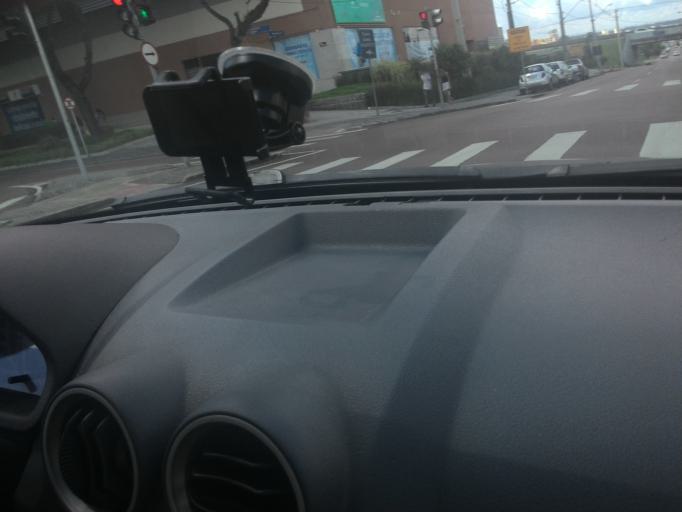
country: BR
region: Parana
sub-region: Pinhais
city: Pinhais
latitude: -25.4524
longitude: -49.2283
